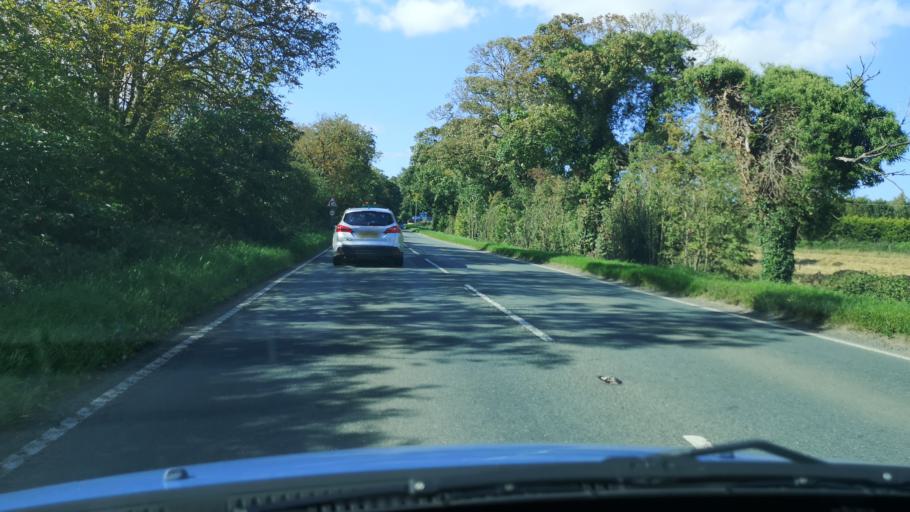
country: GB
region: England
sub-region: North Lincolnshire
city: Belton
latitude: 53.5773
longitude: -0.8189
